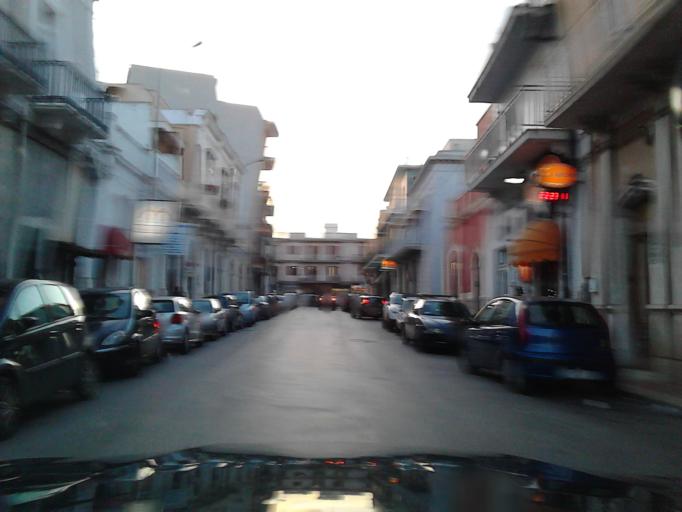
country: IT
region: Apulia
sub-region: Provincia di Bari
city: Valenzano
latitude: 41.0439
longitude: 16.8856
